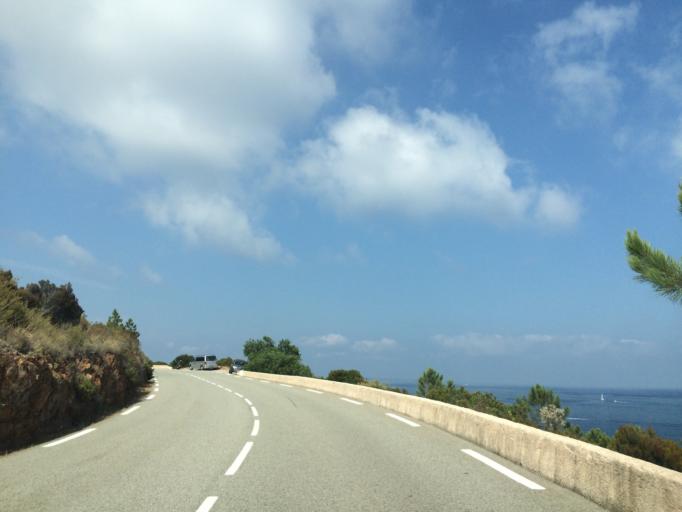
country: FR
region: Provence-Alpes-Cote d'Azur
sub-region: Departement des Alpes-Maritimes
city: Theoule-sur-Mer
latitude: 43.4541
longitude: 6.9205
